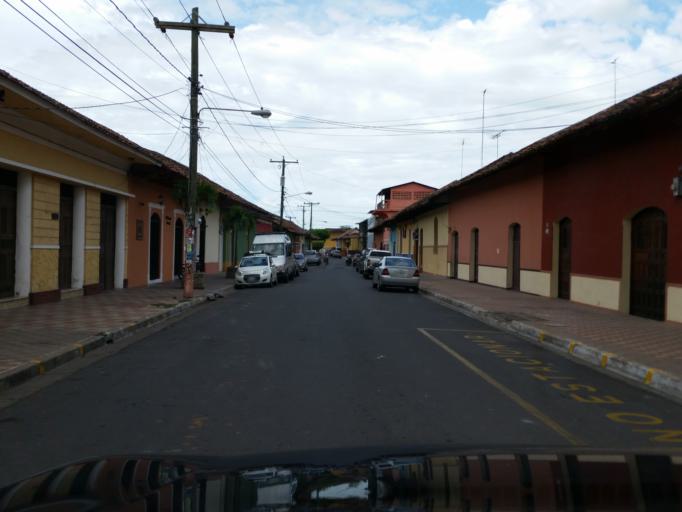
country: NI
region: Granada
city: Granada
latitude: 11.9326
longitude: -85.9548
